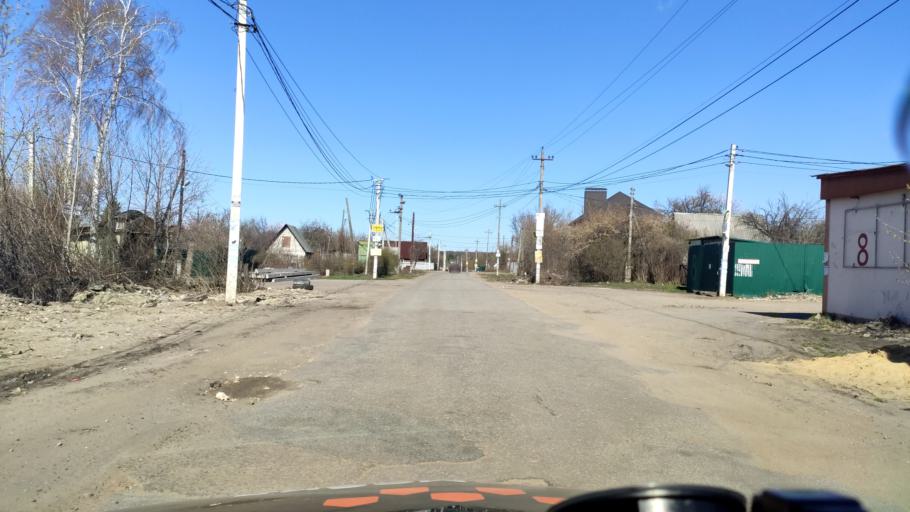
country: RU
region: Voronezj
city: Shilovo
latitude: 51.5989
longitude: 39.1458
